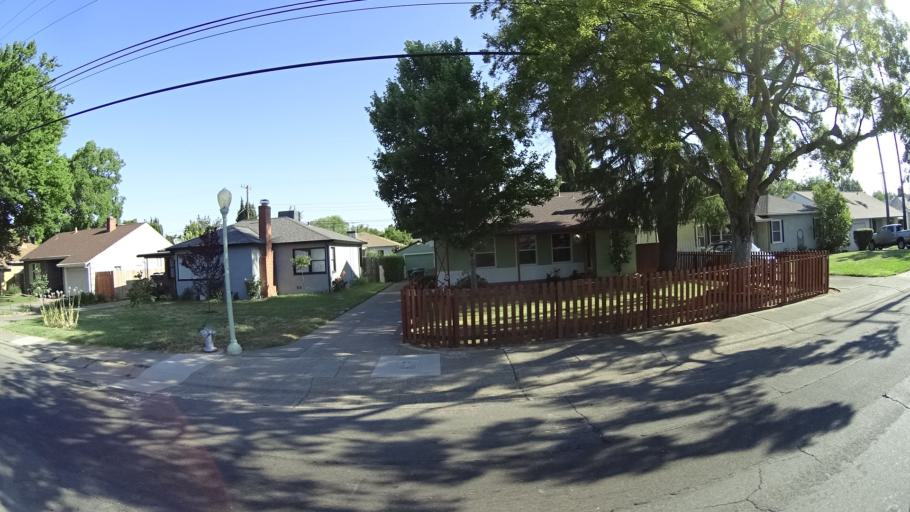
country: US
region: California
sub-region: Sacramento County
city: Parkway
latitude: 38.5395
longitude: -121.4368
